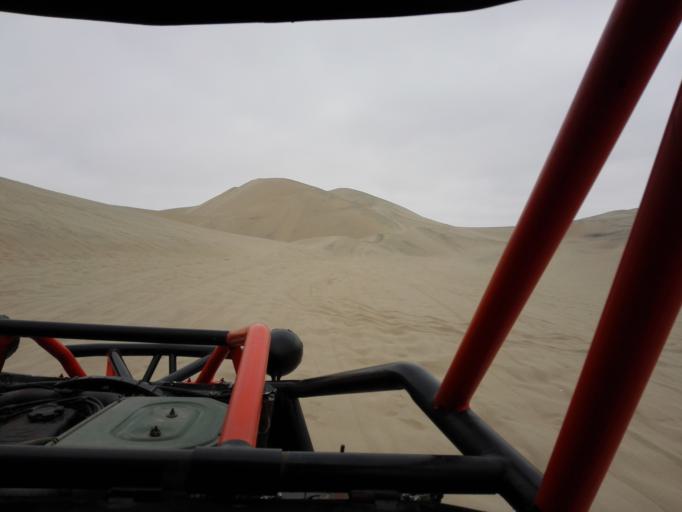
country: PE
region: Ica
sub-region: Provincia de Ica
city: Ica
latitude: -14.0888
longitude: -75.7658
